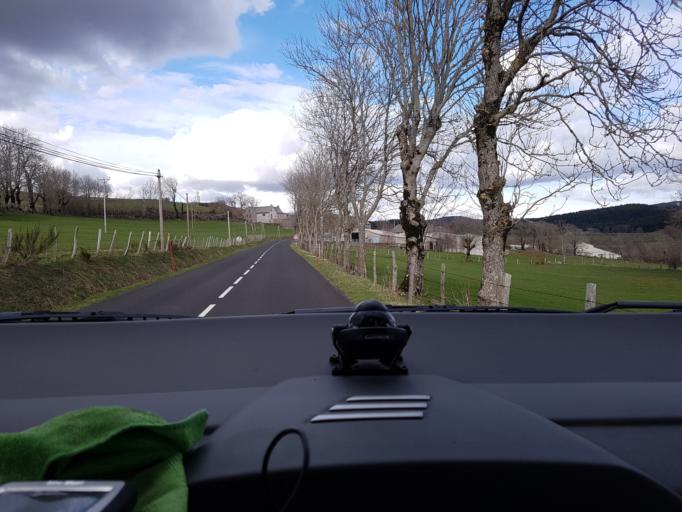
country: FR
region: Midi-Pyrenees
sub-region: Departement de l'Aveyron
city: Laguiole
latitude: 44.6754
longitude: 2.8705
